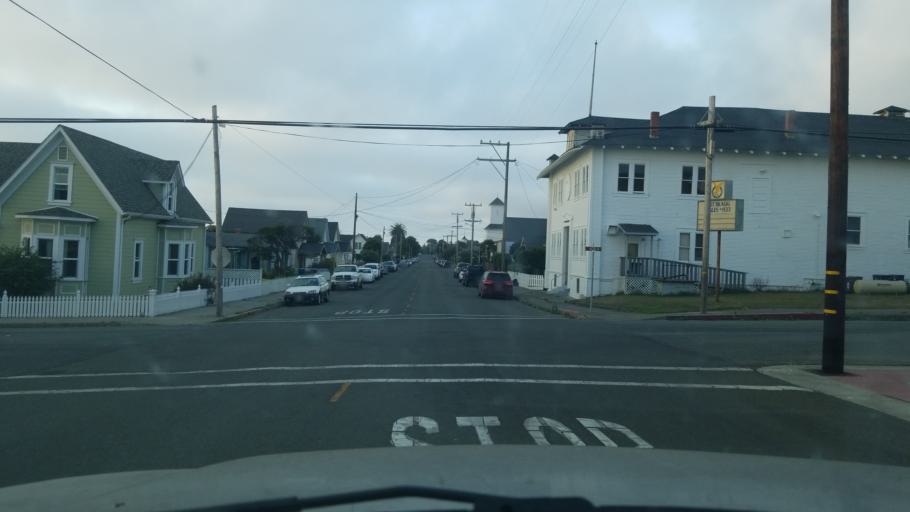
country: US
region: California
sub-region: Mendocino County
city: Fort Bragg
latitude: 39.4426
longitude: -123.7994
